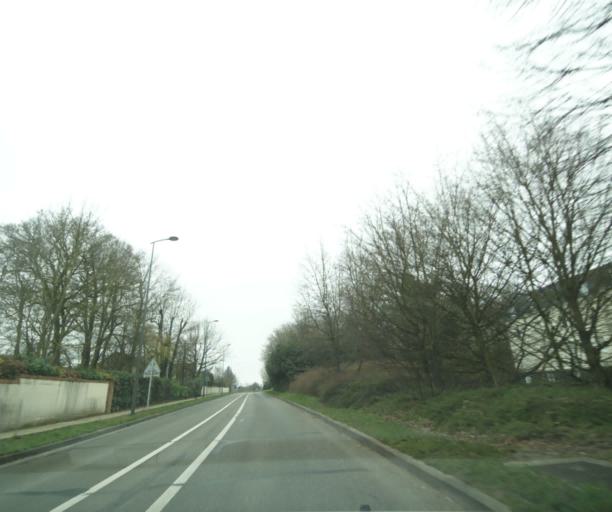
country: FR
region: Ile-de-France
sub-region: Departement du Val-d'Oise
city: Courdimanche
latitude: 49.0440
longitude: 2.0094
